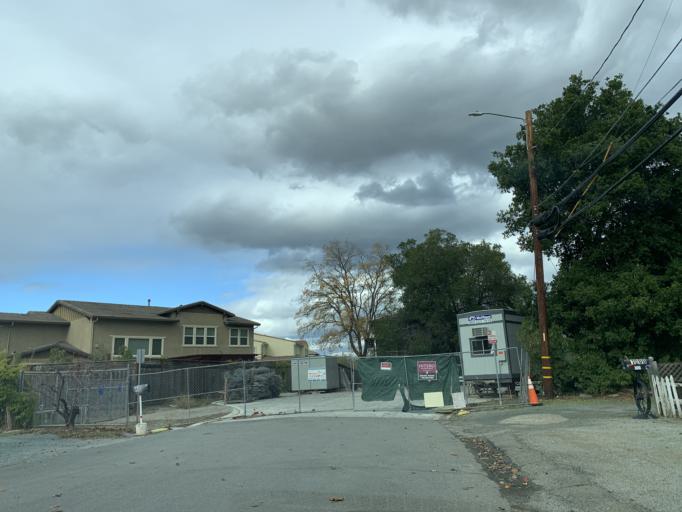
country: US
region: California
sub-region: Santa Clara County
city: Campbell
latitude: 37.2693
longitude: -121.9759
